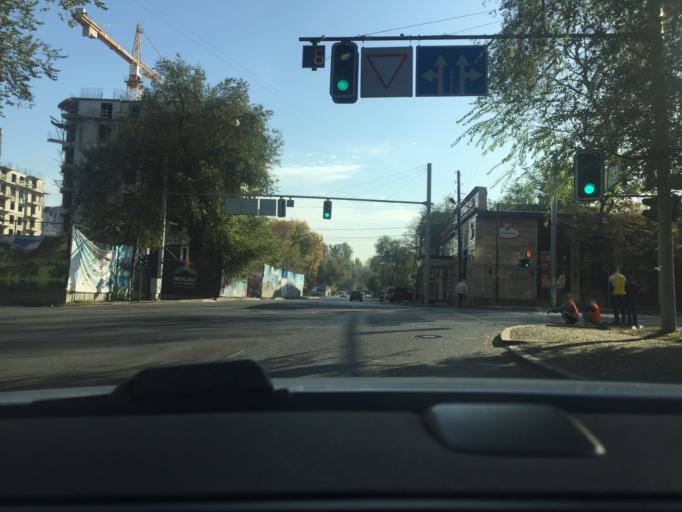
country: KZ
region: Almaty Qalasy
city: Almaty
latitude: 43.2459
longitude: 76.9154
